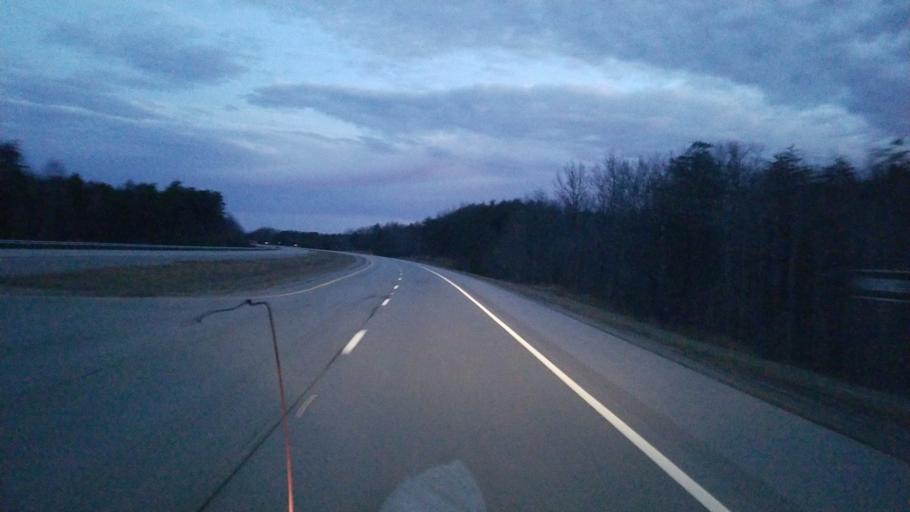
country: US
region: Tennessee
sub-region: Van Buren County
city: Spencer
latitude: 35.6012
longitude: -85.4684
